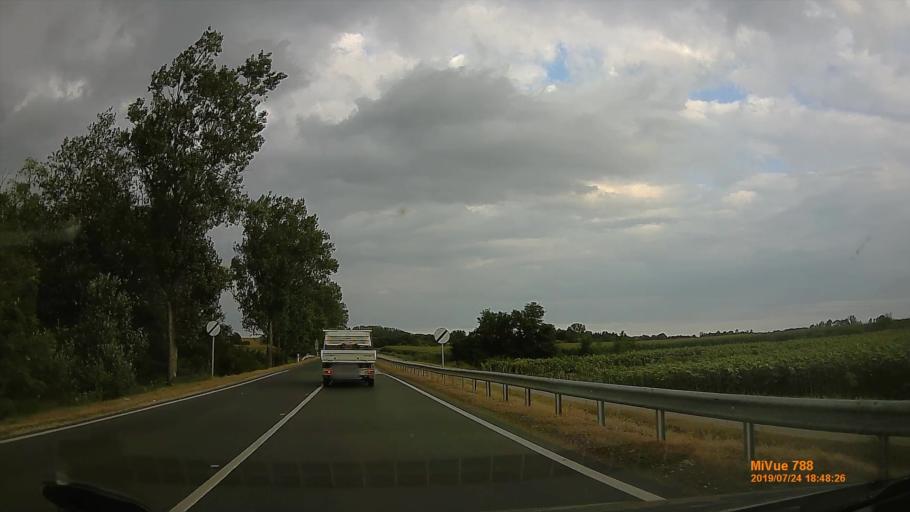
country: HU
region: Szabolcs-Szatmar-Bereg
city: Tiszanagyfalu
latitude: 48.0825
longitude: 21.5000
